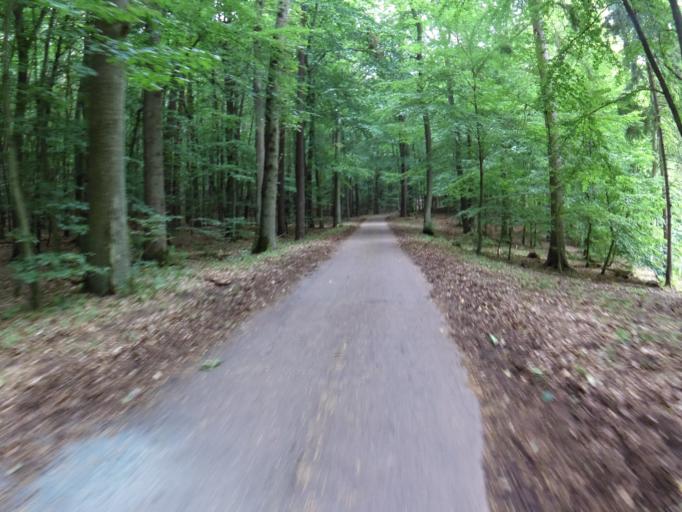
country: DE
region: Mecklenburg-Vorpommern
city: Seebad Heringsdorf
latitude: 53.9059
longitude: 14.1625
